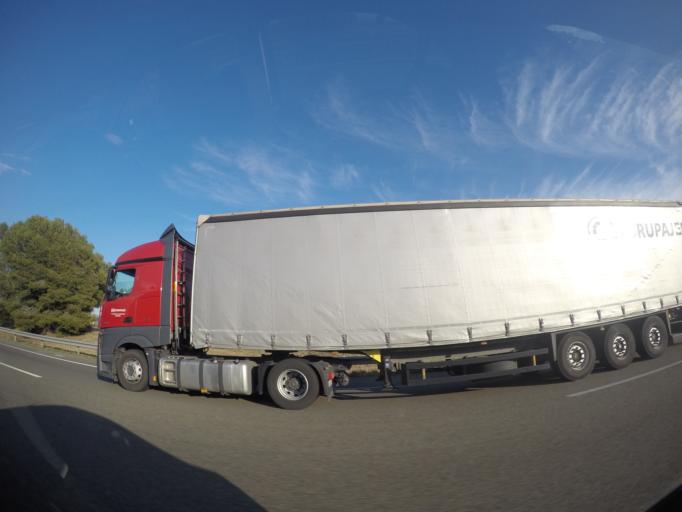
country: ES
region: Catalonia
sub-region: Provincia de Tarragona
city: Sant Jaume dels Domenys
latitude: 41.2975
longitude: 1.6007
